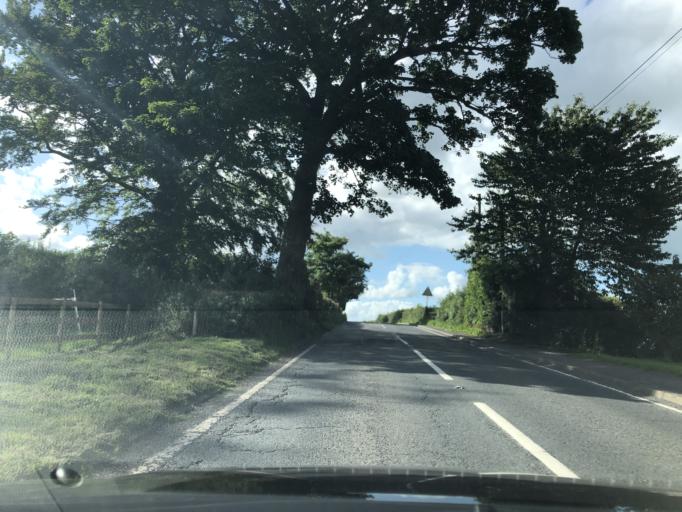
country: GB
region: Northern Ireland
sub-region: Castlereagh District
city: Dundonald
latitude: 54.5716
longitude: -5.7771
